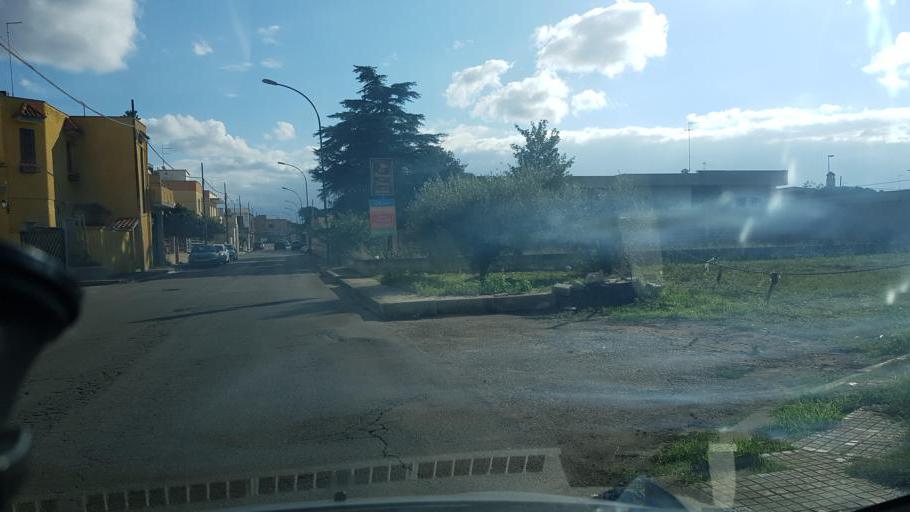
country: IT
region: Apulia
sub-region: Provincia di Lecce
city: Squinzano
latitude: 40.4346
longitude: 18.0317
